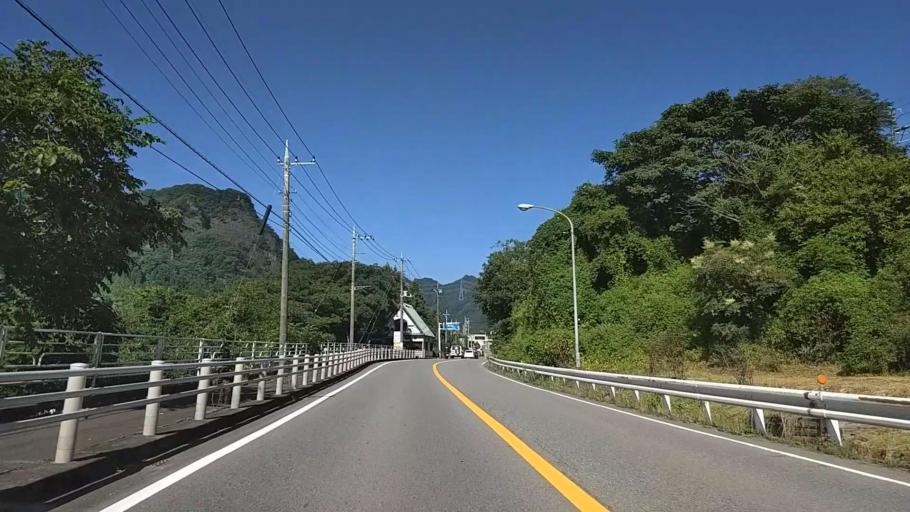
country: JP
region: Gunma
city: Annaka
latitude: 36.3339
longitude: 138.7449
